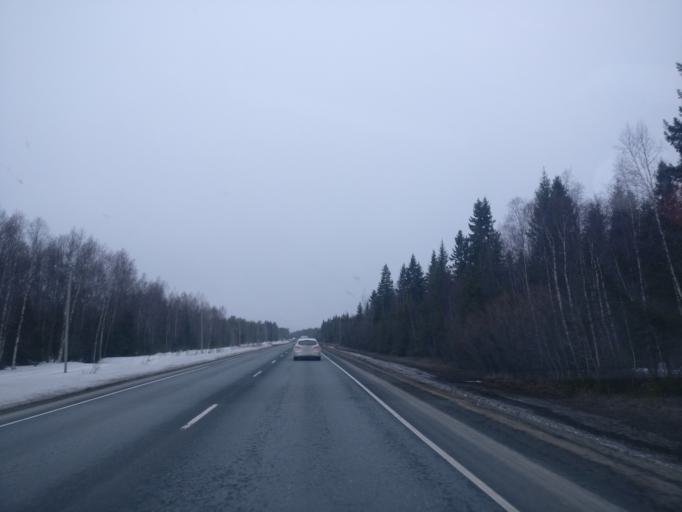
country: FI
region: Lapland
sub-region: Kemi-Tornio
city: Simo
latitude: 65.6713
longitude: 24.9171
